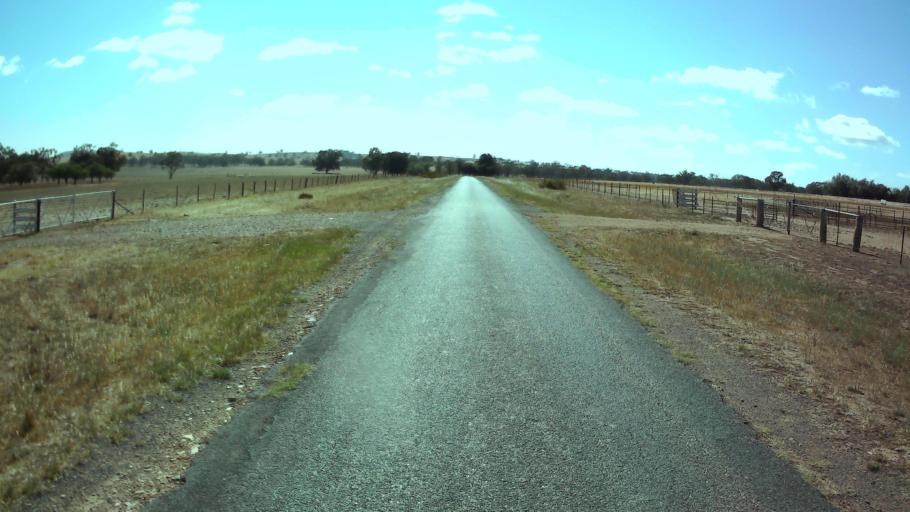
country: AU
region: New South Wales
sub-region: Young
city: Young
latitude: -34.0759
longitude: 148.3609
